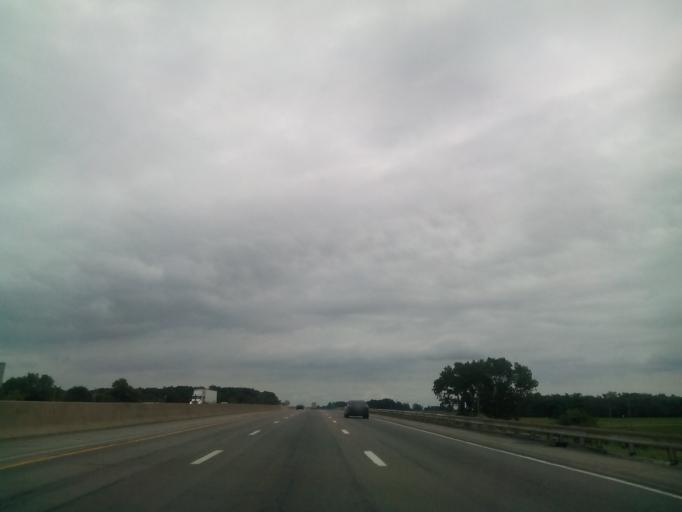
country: US
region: Ohio
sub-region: Huron County
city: Monroeville
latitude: 41.3390
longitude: -82.7502
